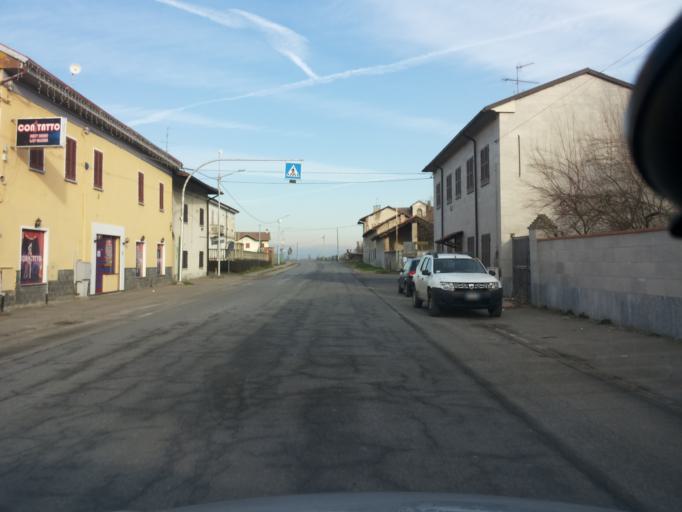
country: IT
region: Piedmont
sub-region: Provincia di Vercelli
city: Oldenico
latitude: 45.4031
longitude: 8.3788
